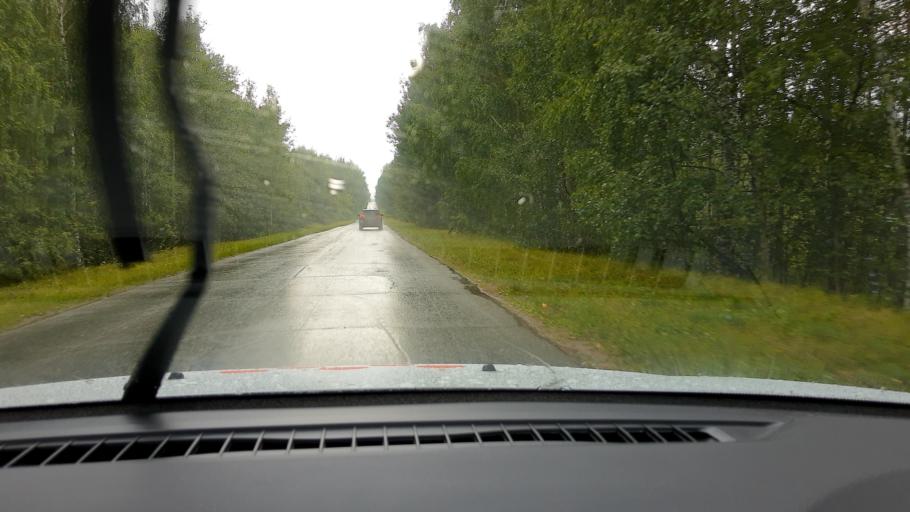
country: RU
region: Nizjnij Novgorod
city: Surovatikha
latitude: 55.9503
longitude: 43.9371
